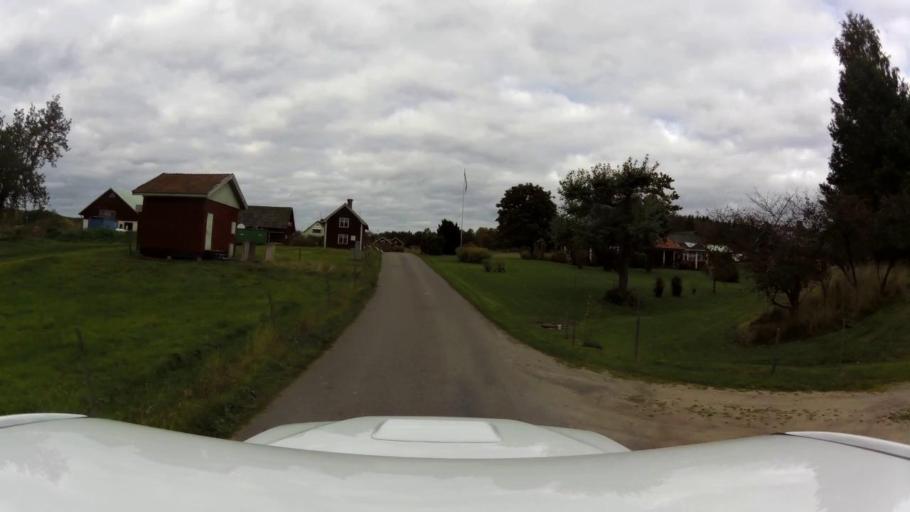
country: SE
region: OEstergoetland
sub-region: Kinda Kommun
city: Rimforsa
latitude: 58.1981
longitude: 15.5778
